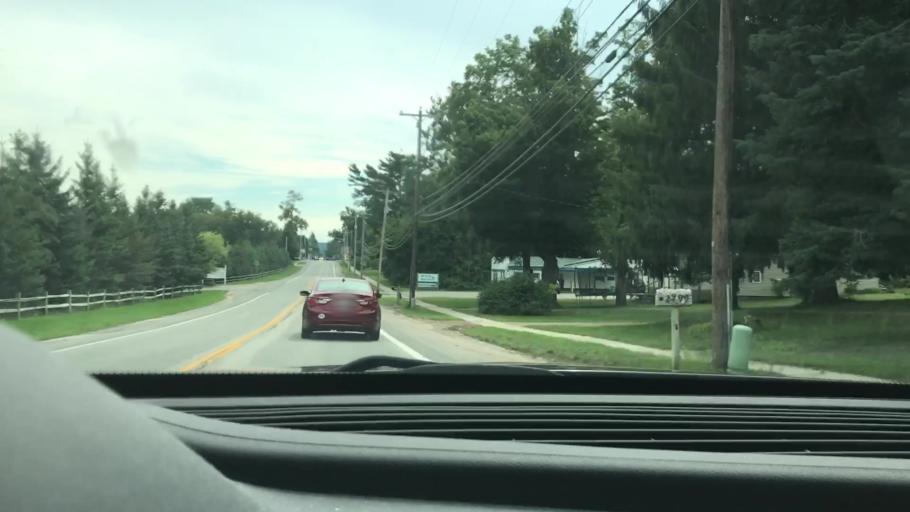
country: US
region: Michigan
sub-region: Antrim County
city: Bellaire
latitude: 45.0758
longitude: -85.2642
